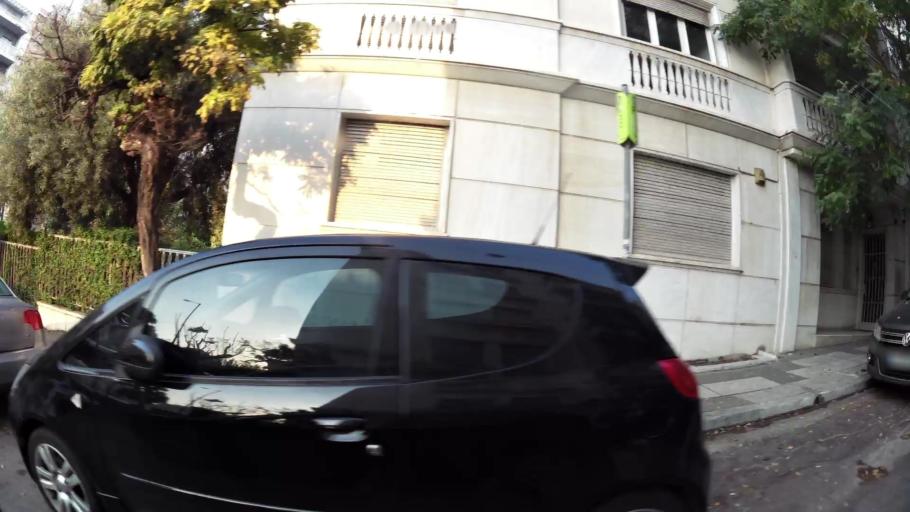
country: GR
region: Attica
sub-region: Nomarchia Athinas
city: Vyronas
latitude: 37.9756
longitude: 23.7420
